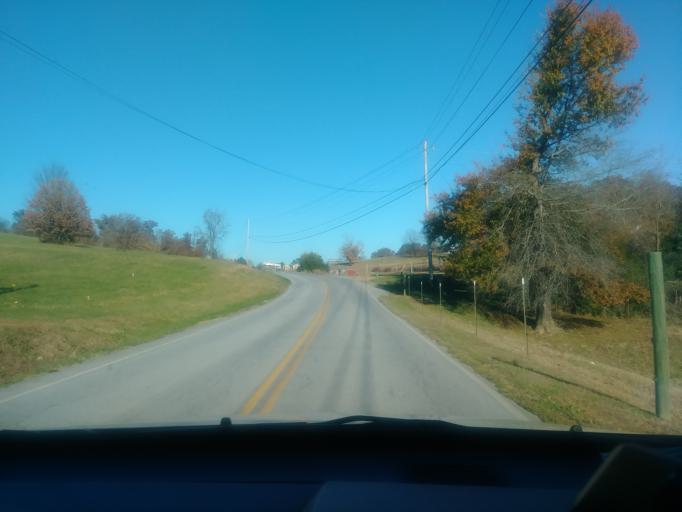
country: US
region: Tennessee
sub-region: Greene County
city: Greeneville
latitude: 36.0743
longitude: -82.8838
